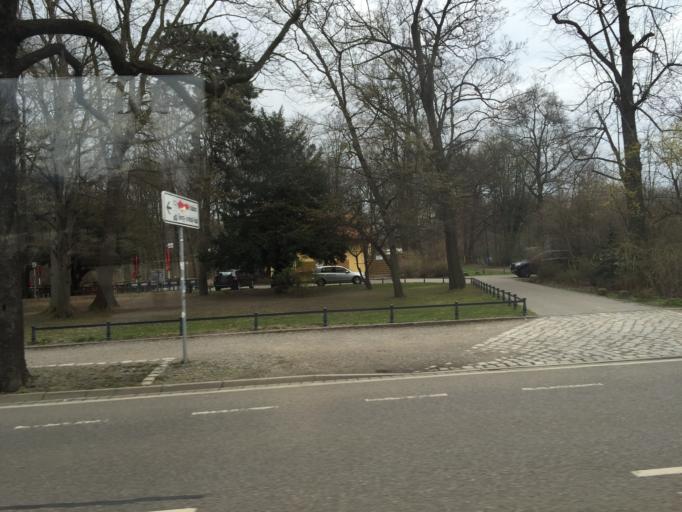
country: DE
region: Saxony
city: Dresden
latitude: 51.0417
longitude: 13.7504
